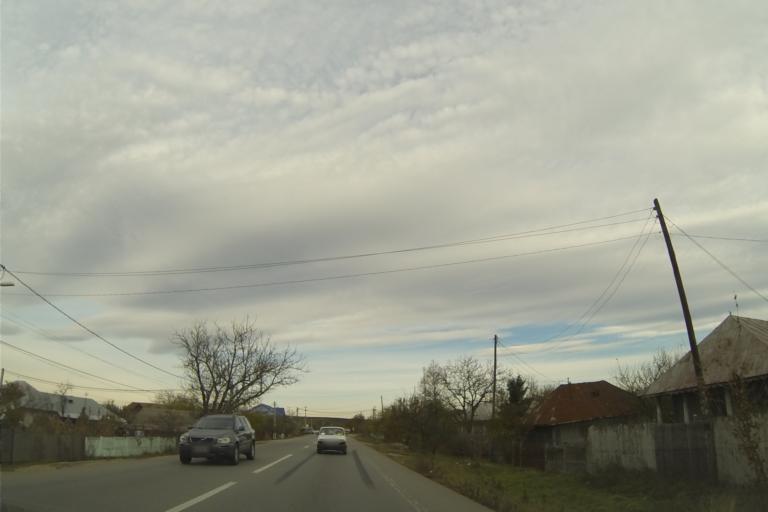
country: RO
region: Olt
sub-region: Comuna Scornicesti
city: Margineni Slobozia
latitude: 44.5467
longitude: 24.5481
